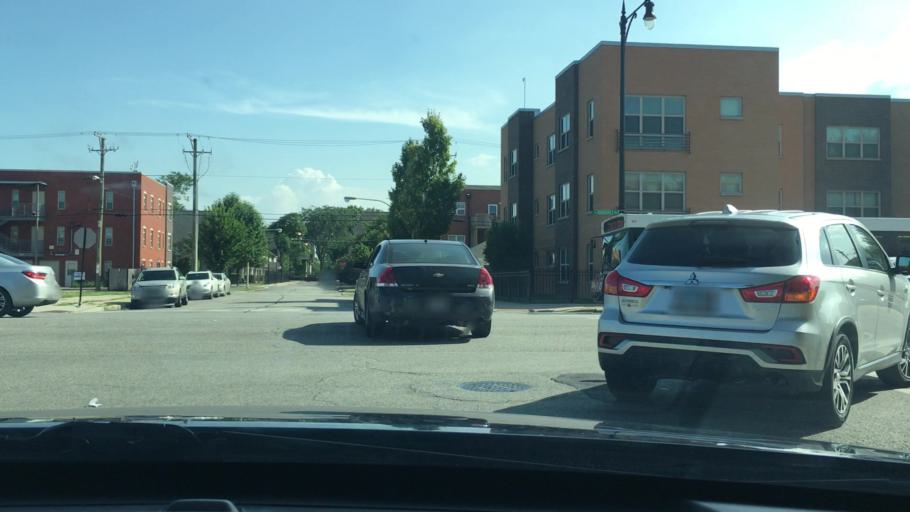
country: US
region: Illinois
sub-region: Cook County
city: Chicago
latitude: 41.8671
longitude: -87.6592
